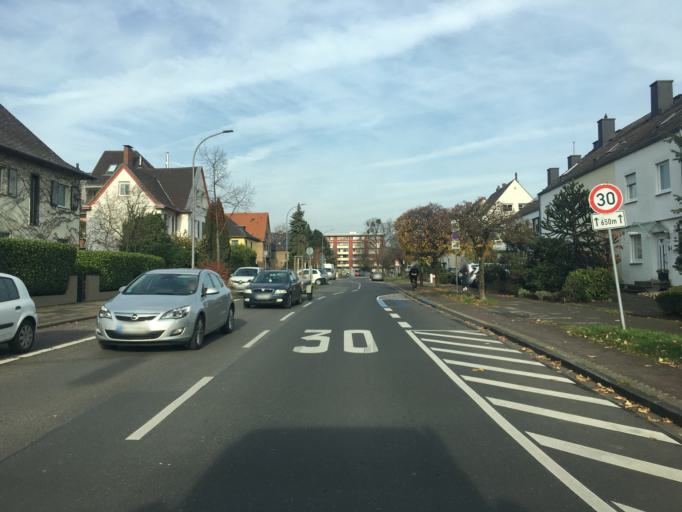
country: DE
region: North Rhine-Westphalia
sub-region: Regierungsbezirk Koln
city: Rath
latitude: 50.9518
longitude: 7.1027
